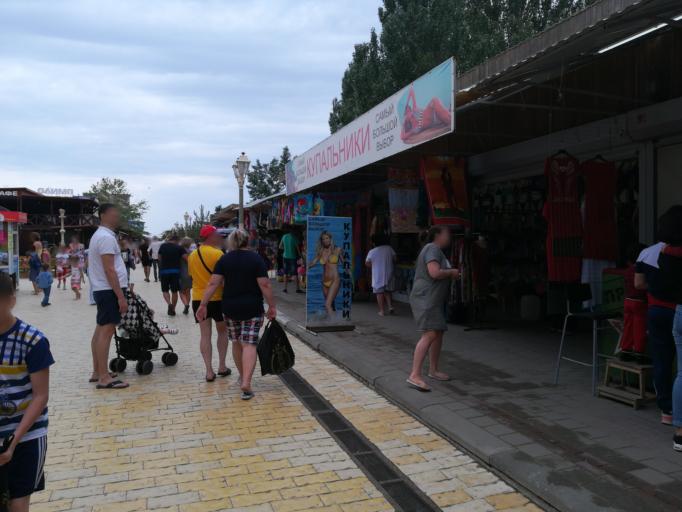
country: RU
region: Krasnodarskiy
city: Vityazevo
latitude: 44.9850
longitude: 37.2534
